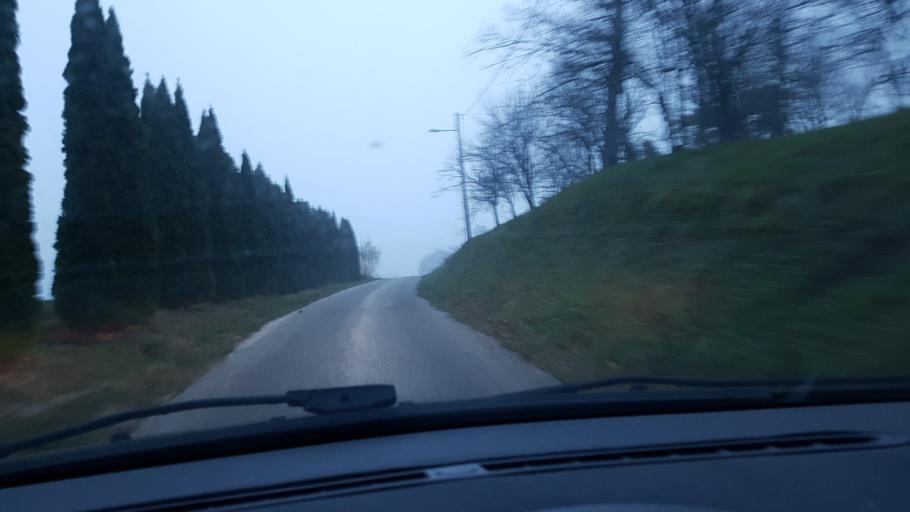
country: HR
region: Krapinsko-Zagorska
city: Pregrada
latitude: 46.1916
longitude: 15.7263
